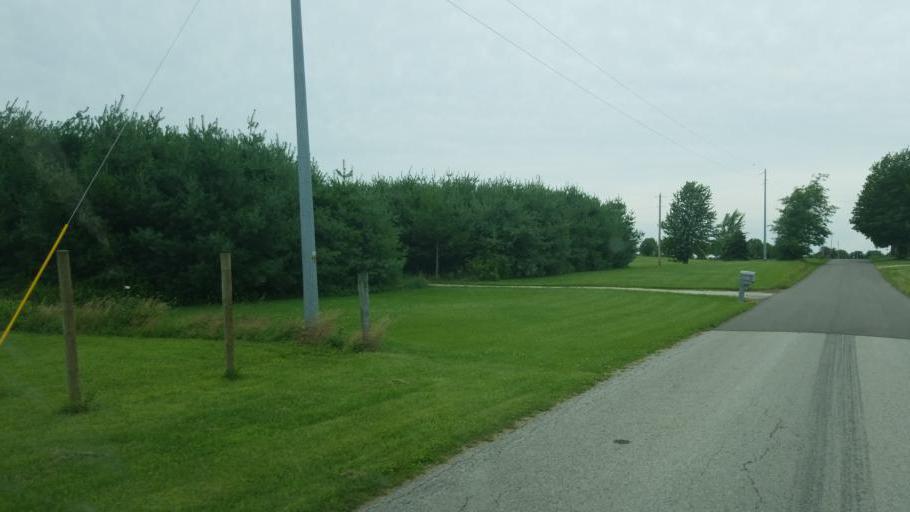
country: US
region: Ohio
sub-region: Licking County
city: Johnstown
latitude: 40.2272
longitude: -82.5877
